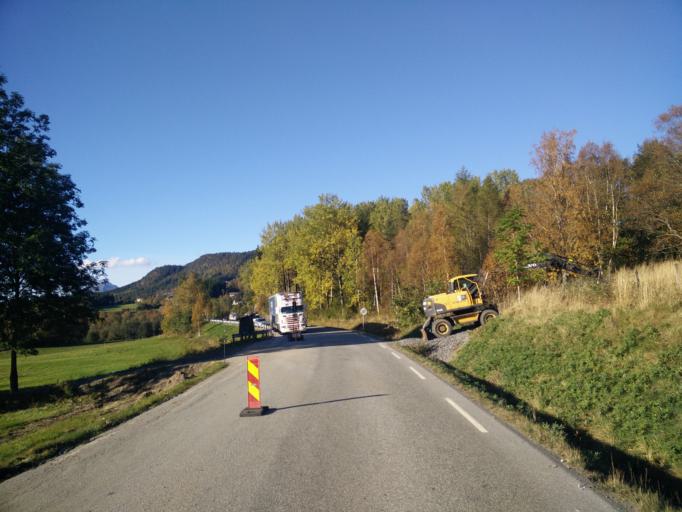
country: NO
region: More og Romsdal
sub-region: Halsa
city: Liaboen
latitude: 63.1127
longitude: 8.3253
